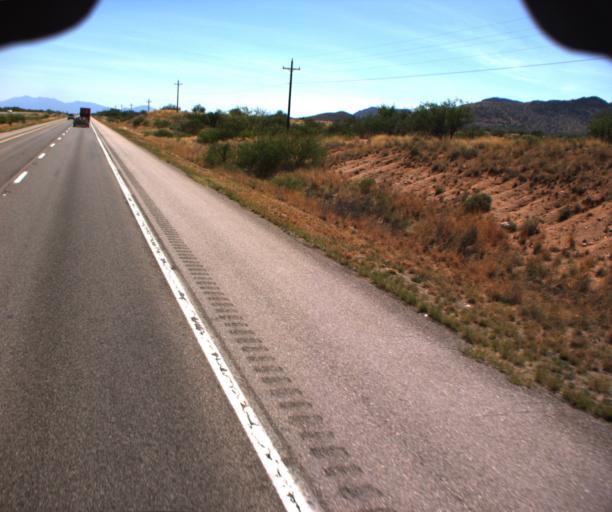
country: US
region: Arizona
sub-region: Cochise County
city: Whetstone
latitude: 31.8741
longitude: -110.3414
